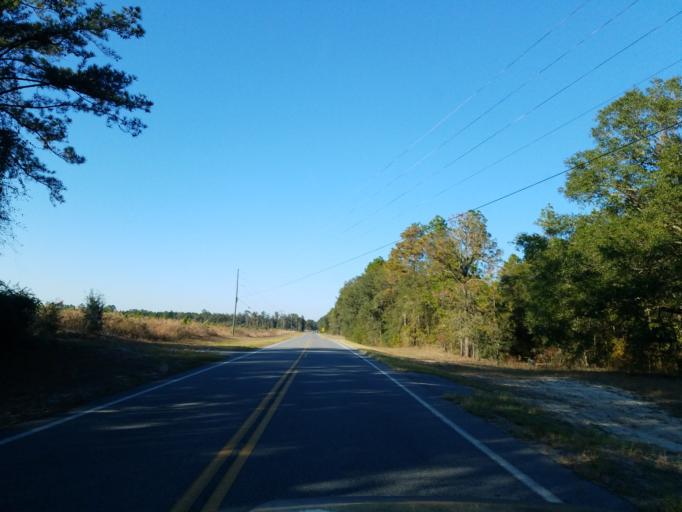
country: US
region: Georgia
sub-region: Echols County
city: Statenville
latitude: 30.6885
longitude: -83.0617
